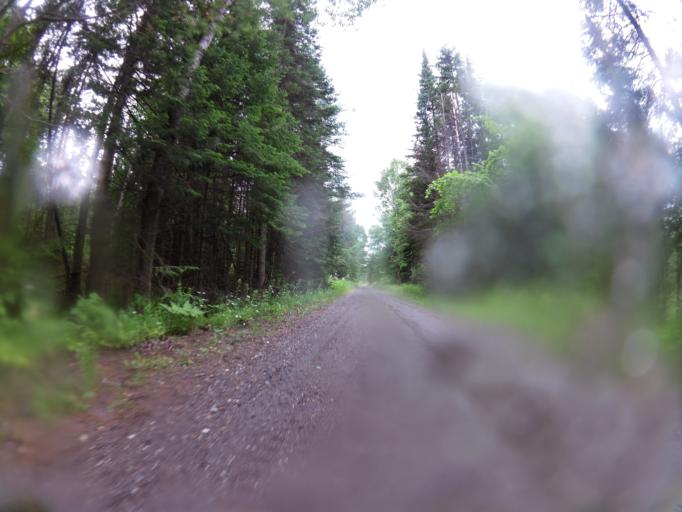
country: CA
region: Ontario
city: Renfrew
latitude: 45.0778
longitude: -76.7205
